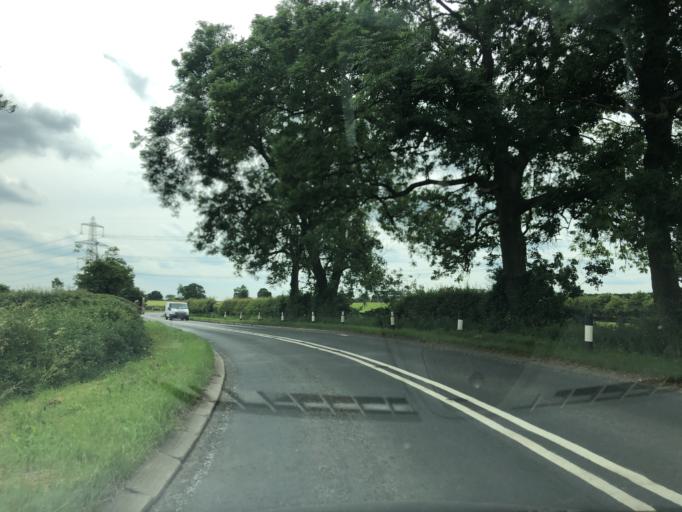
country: GB
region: England
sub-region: North Yorkshire
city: Thirsk
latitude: 54.2348
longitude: -1.2716
